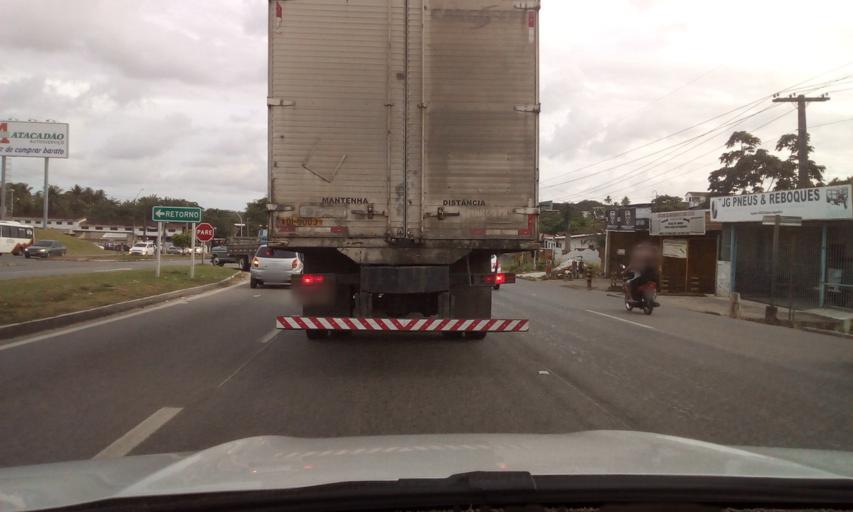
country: BR
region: Pernambuco
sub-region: Abreu E Lima
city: Abreu e Lima
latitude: -7.8794
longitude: -34.9054
